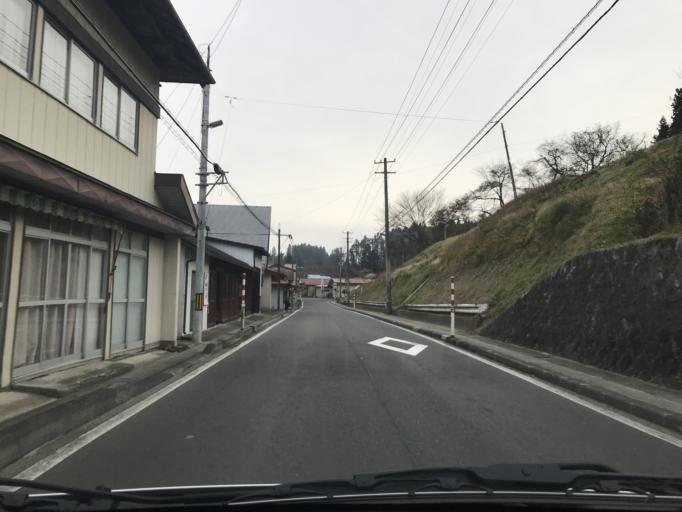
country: JP
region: Iwate
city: Kitakami
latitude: 39.2864
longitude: 141.2621
